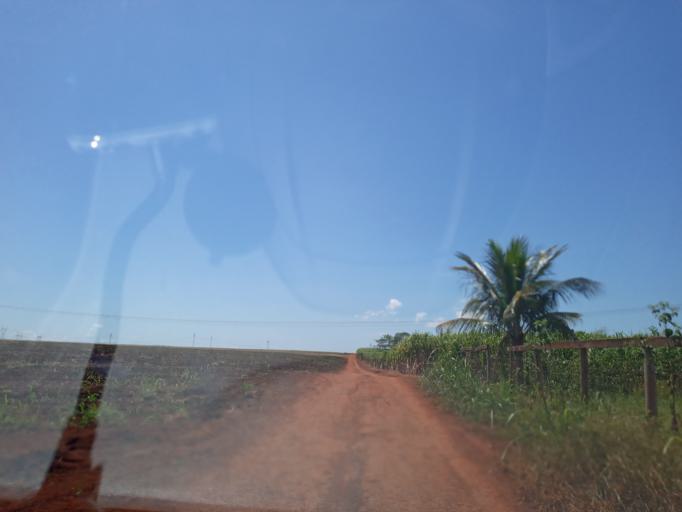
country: BR
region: Goias
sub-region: Itumbiara
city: Itumbiara
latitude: -18.4405
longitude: -49.1338
